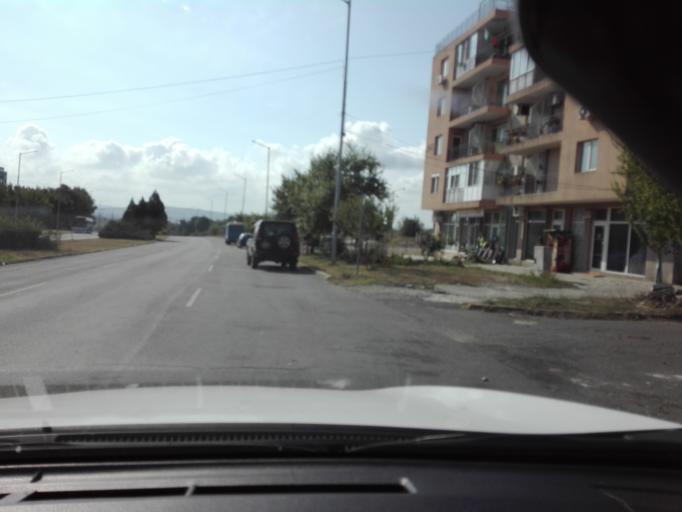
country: BG
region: Burgas
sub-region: Obshtina Burgas
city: Burgas
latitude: 42.4521
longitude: 27.4209
